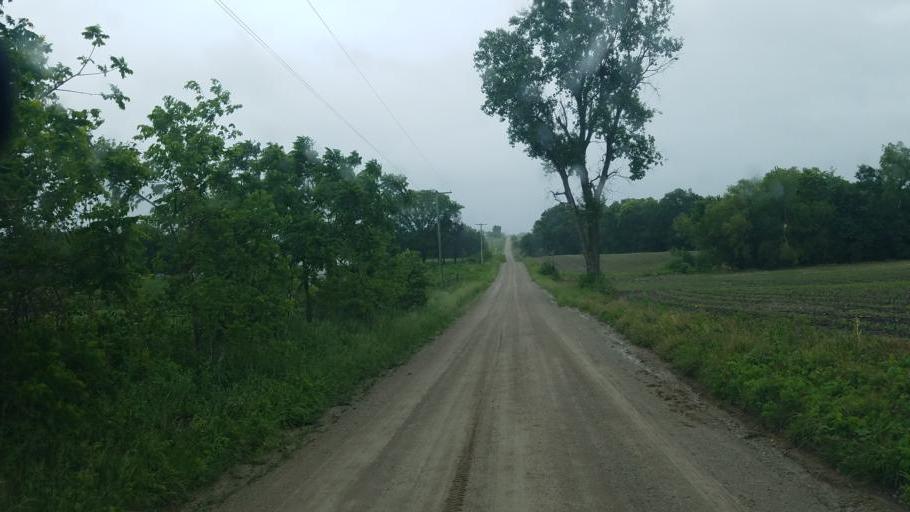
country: US
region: Missouri
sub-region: Carroll County
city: Carrollton
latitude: 39.4707
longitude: -93.4728
